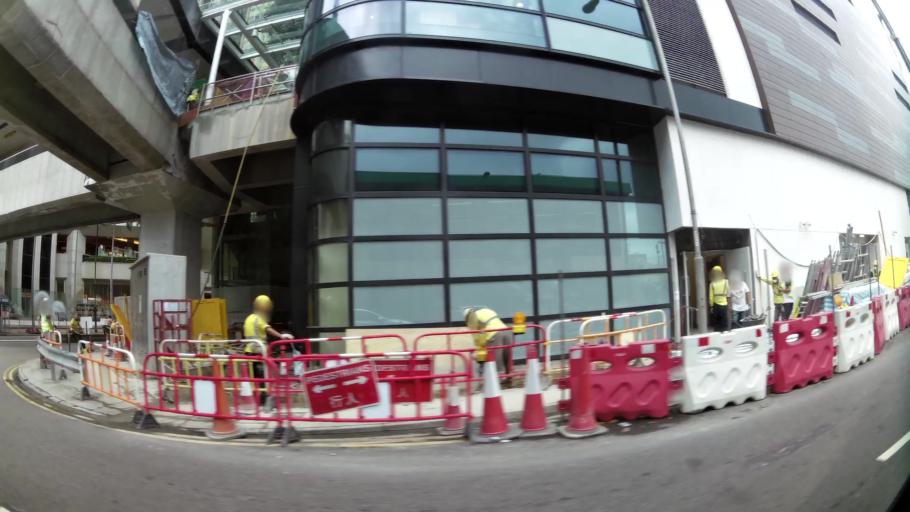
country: HK
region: Wanchai
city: Wan Chai
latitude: 22.2810
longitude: 114.1772
